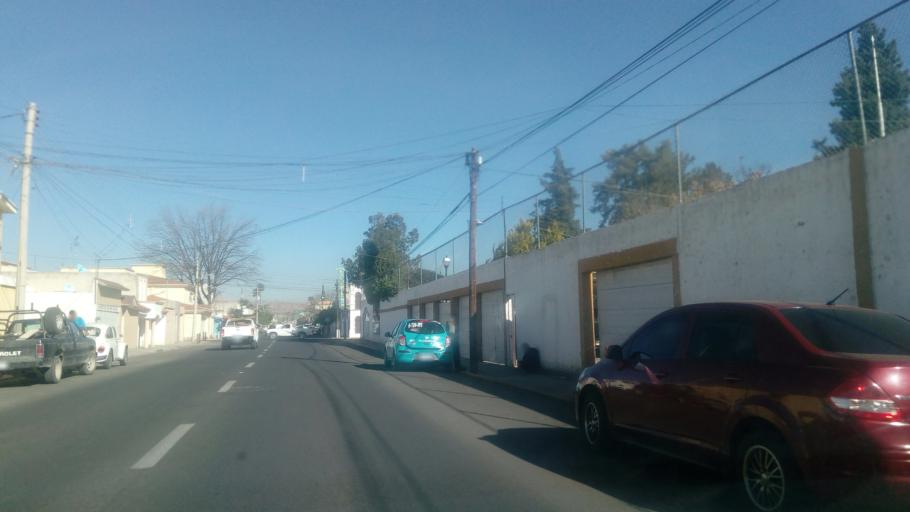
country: MX
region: Durango
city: Victoria de Durango
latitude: 24.0307
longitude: -104.6589
